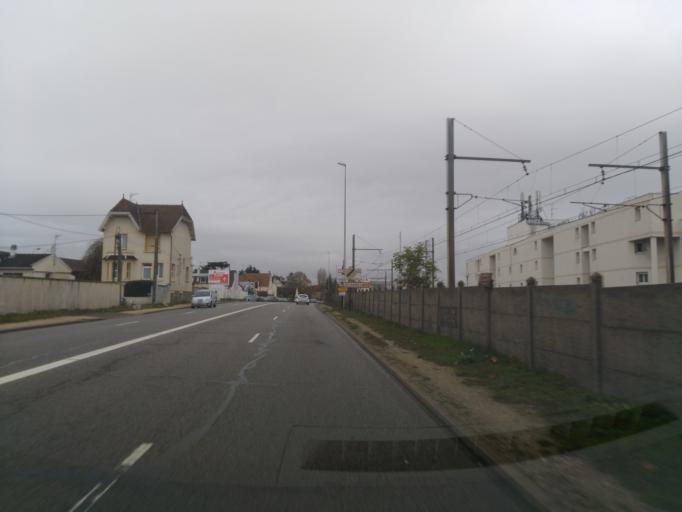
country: FR
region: Ile-de-France
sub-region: Departement des Yvelines
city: Villepreux
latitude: 48.8222
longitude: 1.9955
